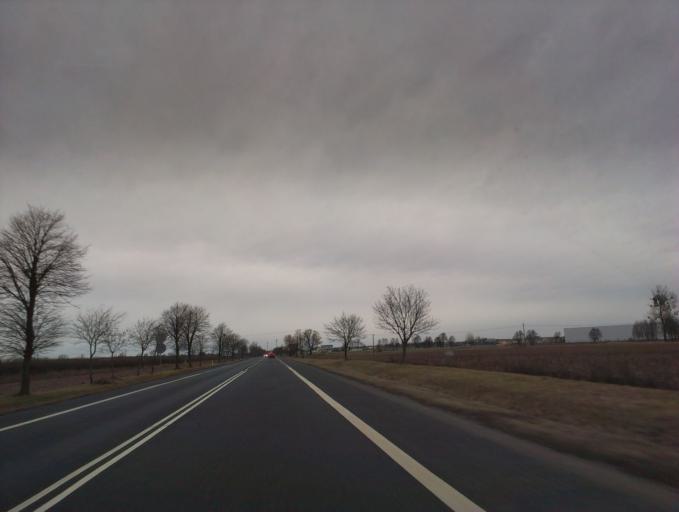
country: PL
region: Greater Poland Voivodeship
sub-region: Powiat chodzieski
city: Budzyn
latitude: 52.8734
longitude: 16.9752
